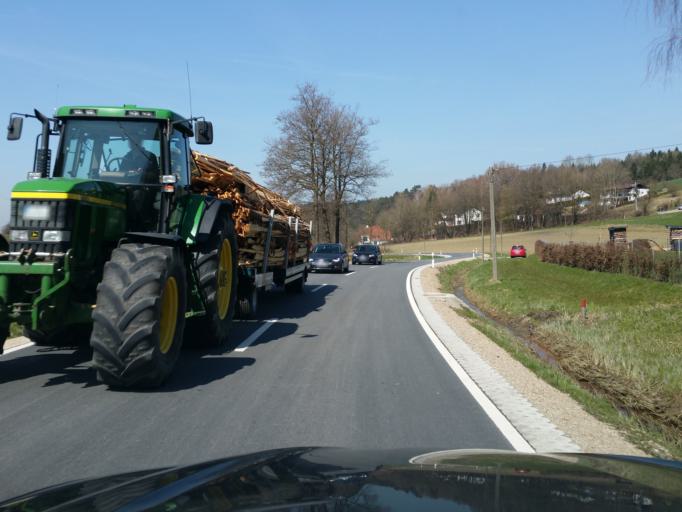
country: DE
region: Bavaria
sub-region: Upper Bavaria
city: Kirchberg
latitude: 48.4478
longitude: 12.0481
